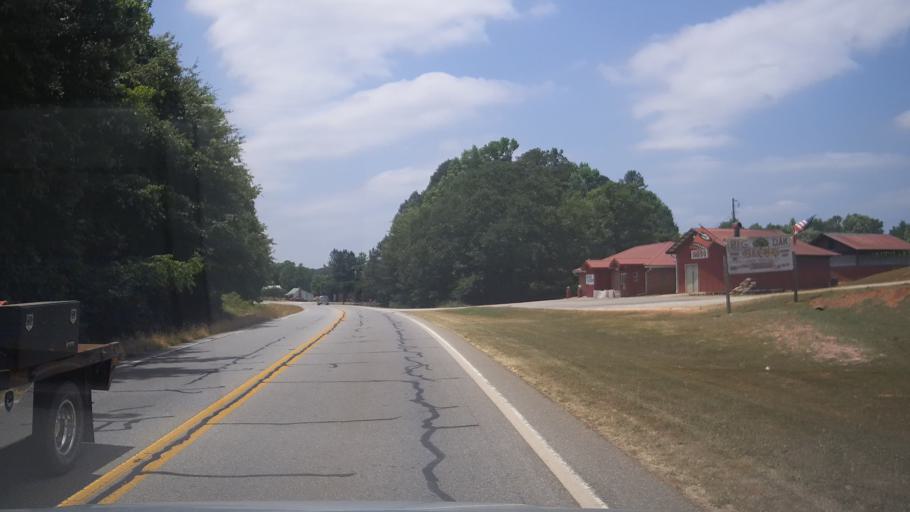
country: US
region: Georgia
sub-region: Jackson County
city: Commerce
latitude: 34.1942
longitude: -83.4176
